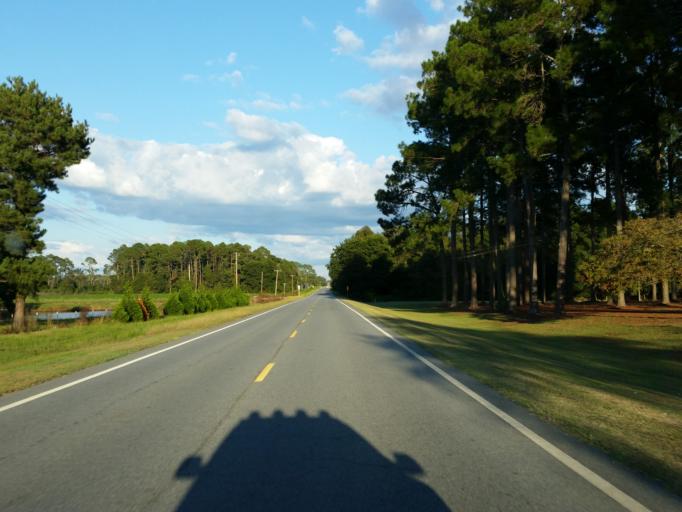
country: US
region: Georgia
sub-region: Dooly County
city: Vienna
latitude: 32.0862
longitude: -83.7540
